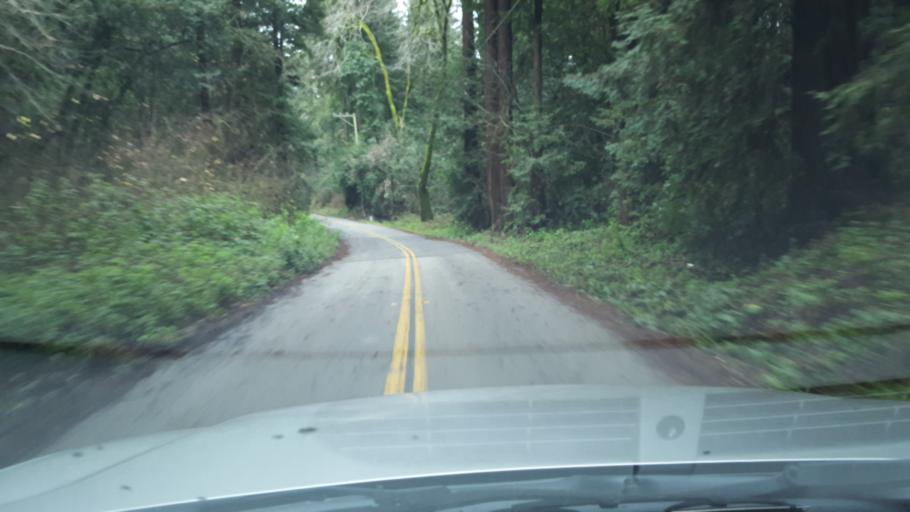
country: US
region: California
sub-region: Santa Cruz County
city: Amesti
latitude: 37.0018
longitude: -121.7465
